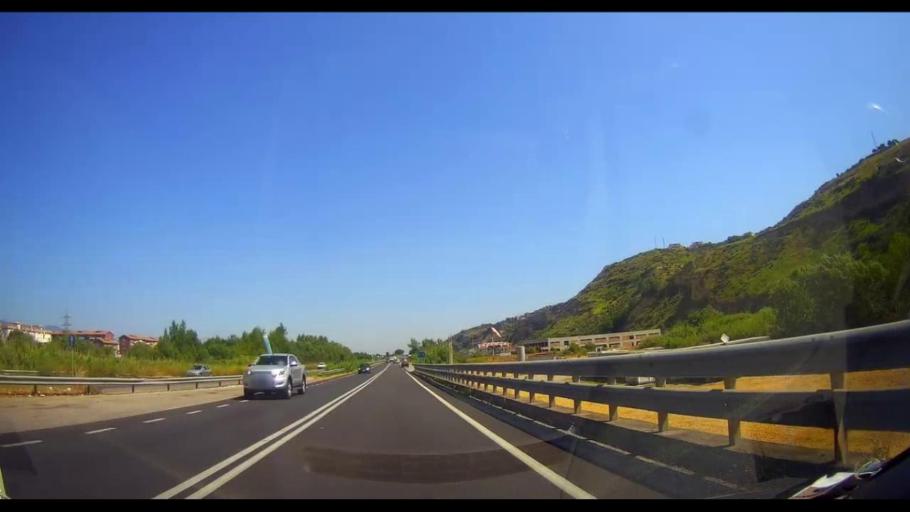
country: IT
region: Calabria
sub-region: Provincia di Cosenza
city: Cosenza
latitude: 39.3030
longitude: 16.2641
